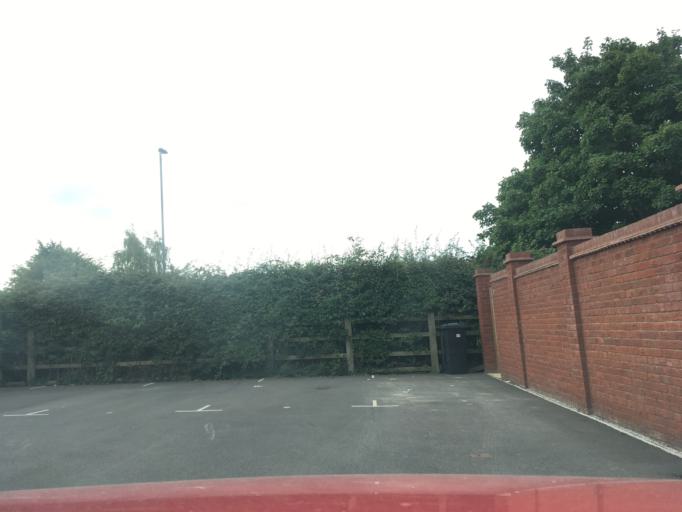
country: GB
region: England
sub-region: South Gloucestershire
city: Thornbury
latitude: 51.6186
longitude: -2.5104
